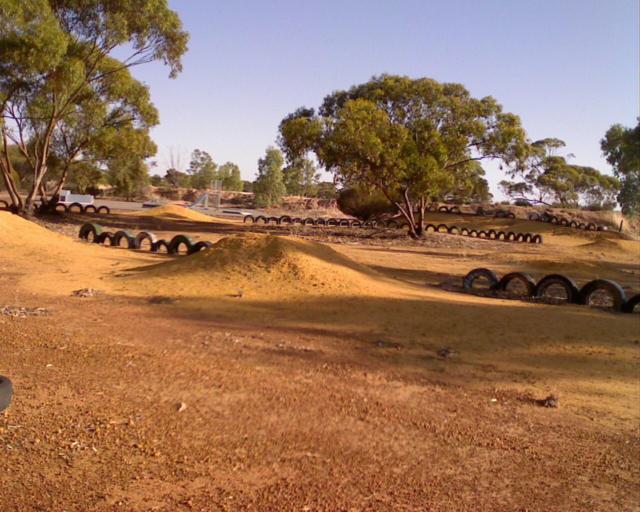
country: AU
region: Western Australia
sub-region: Merredin
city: Merredin
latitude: -31.1123
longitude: 117.7943
